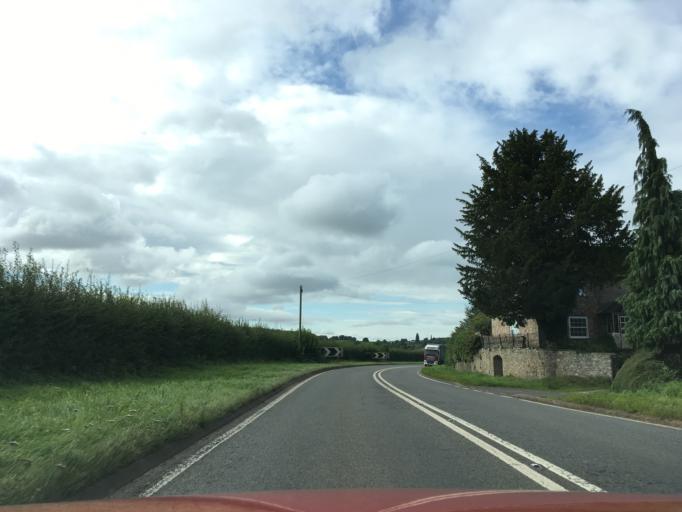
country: GB
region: Wales
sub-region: Monmouthshire
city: Chepstow
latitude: 51.6605
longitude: -2.6371
